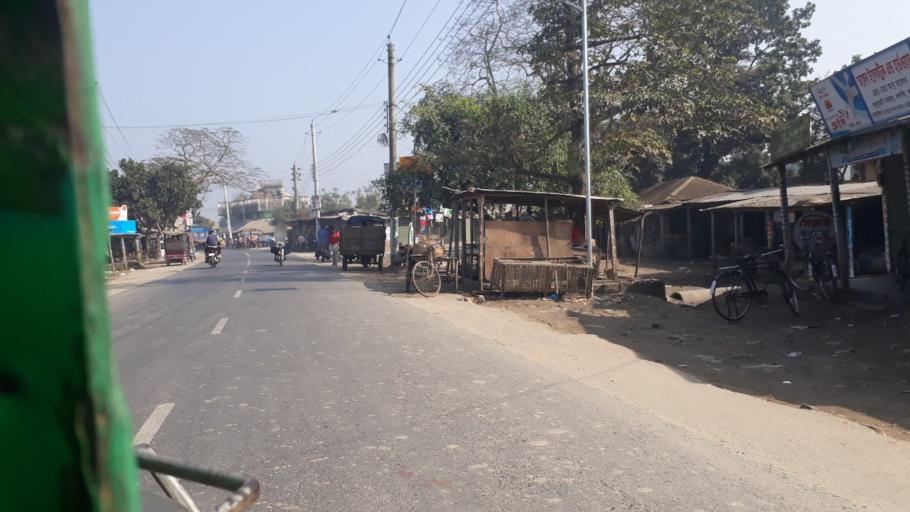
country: BD
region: Khulna
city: Kushtia
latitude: 23.8719
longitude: 89.0734
